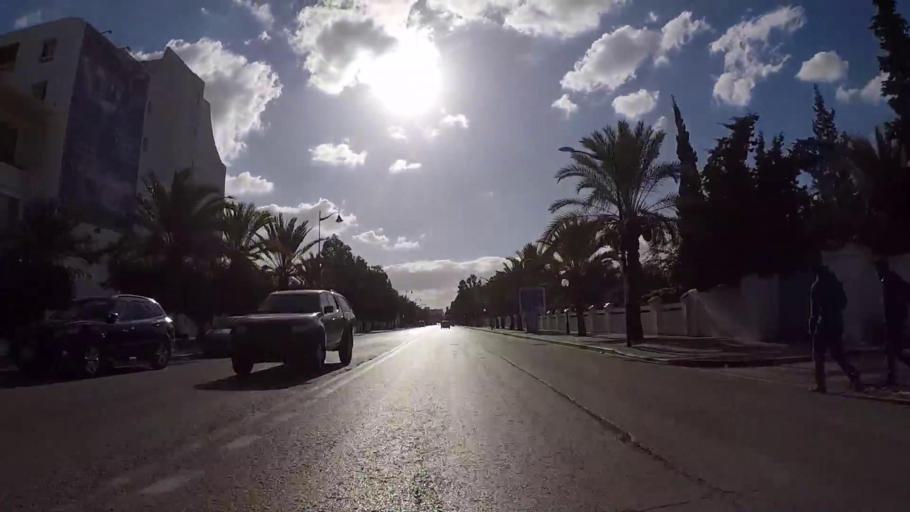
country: TN
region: Nabul
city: Al Hammamat
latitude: 36.3746
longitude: 10.5414
